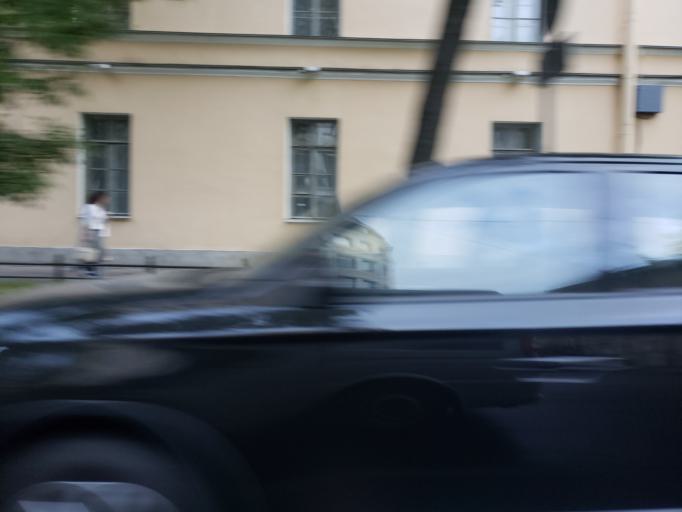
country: RU
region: St.-Petersburg
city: Vasyl'evsky Ostrov
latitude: 59.9352
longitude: 30.2777
